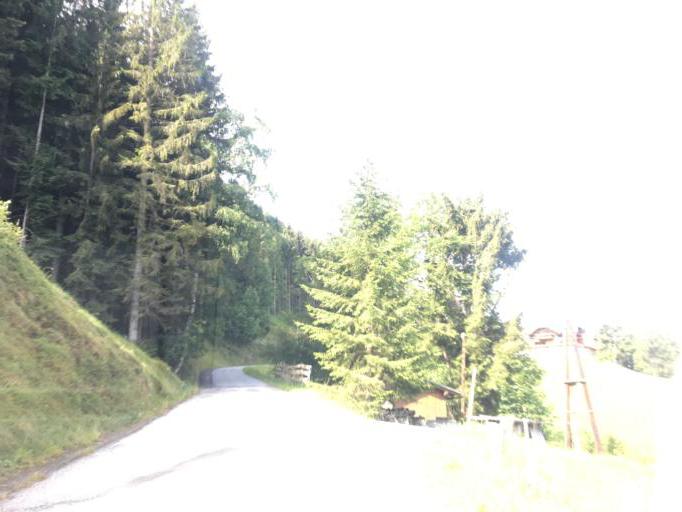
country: AT
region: Styria
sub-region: Politischer Bezirk Liezen
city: Schladming
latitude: 47.3842
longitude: 13.6602
